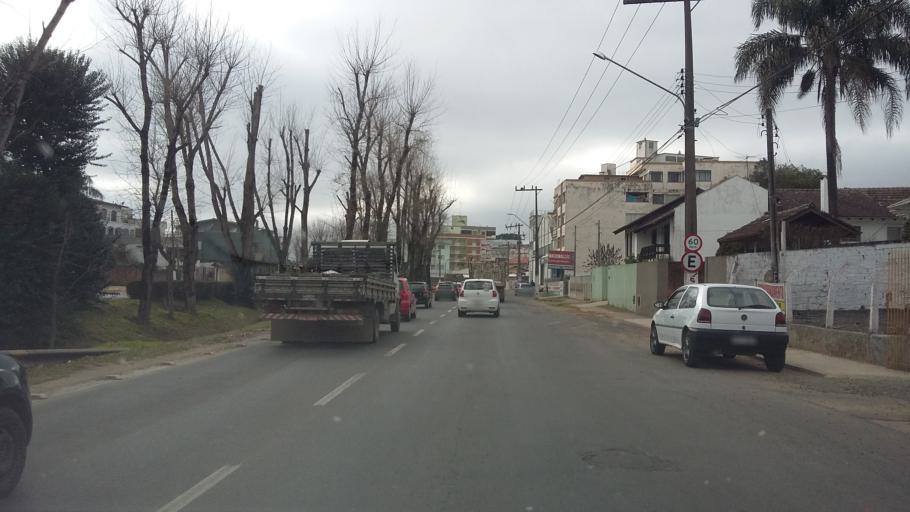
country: BR
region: Santa Catarina
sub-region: Lages
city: Lages
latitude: -27.8110
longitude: -50.3285
